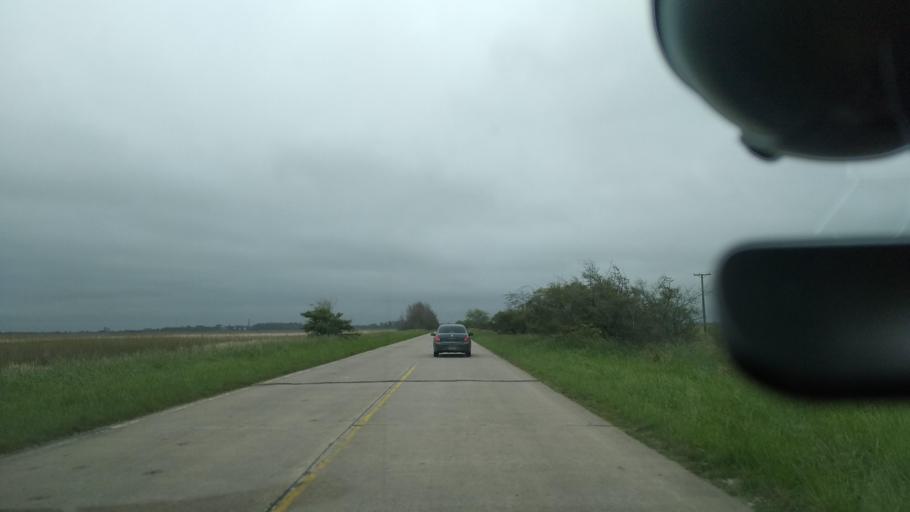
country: AR
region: Buenos Aires
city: Veronica
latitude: -35.5589
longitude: -57.3036
